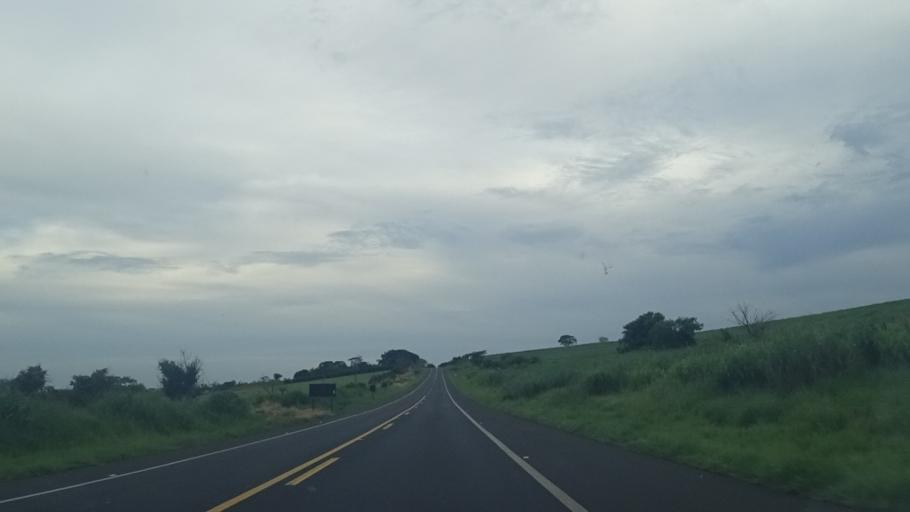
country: BR
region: Sao Paulo
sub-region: Martinopolis
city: Martinopolis
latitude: -22.0968
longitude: -51.1408
